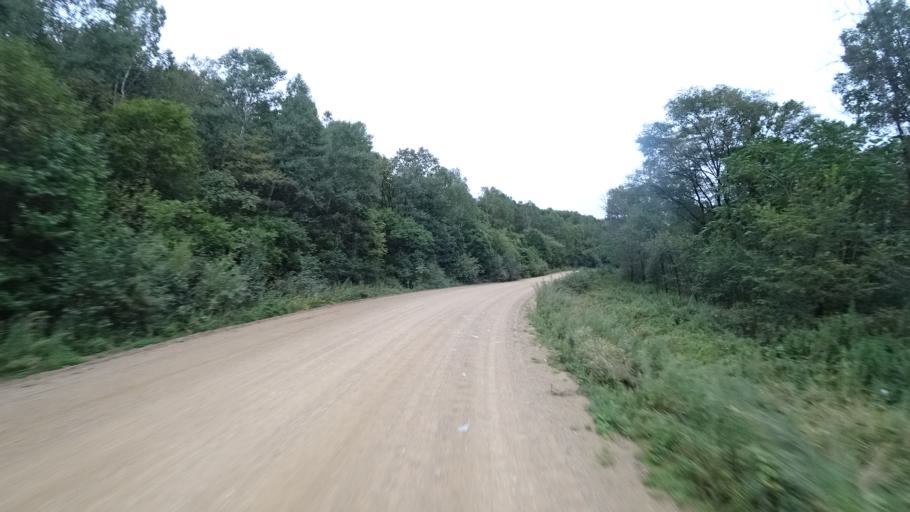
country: RU
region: Primorskiy
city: Rettikhovka
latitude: 44.1807
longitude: 132.8559
